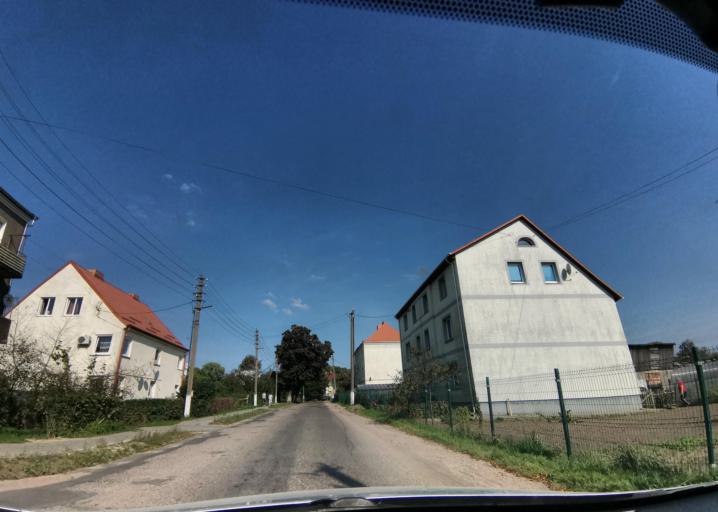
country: RU
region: Kaliningrad
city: Neman
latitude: 55.0325
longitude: 22.0404
